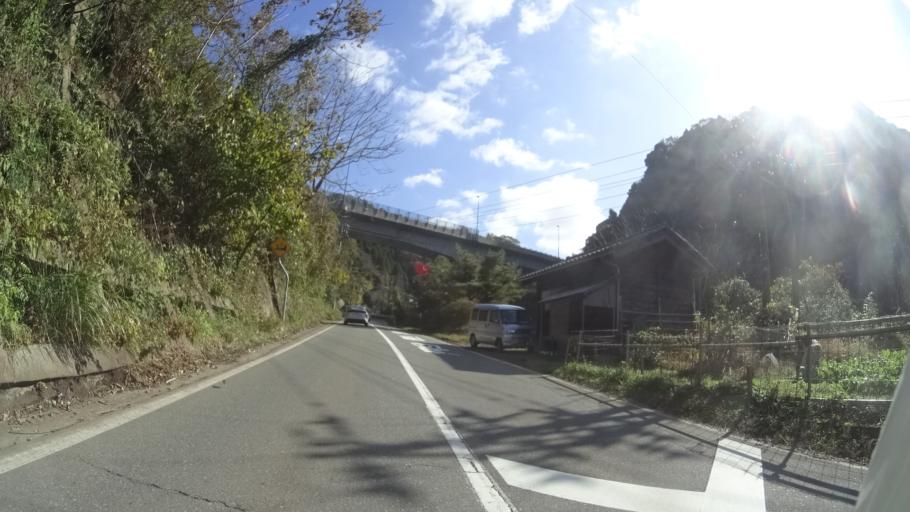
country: JP
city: Asahi
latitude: 35.9602
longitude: 135.9950
